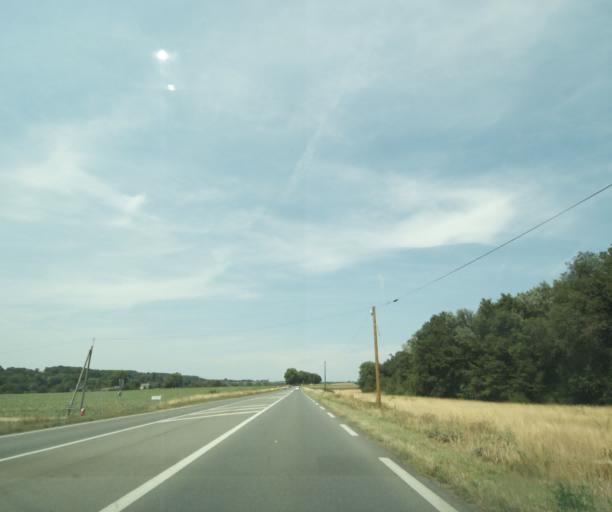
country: FR
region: Poitou-Charentes
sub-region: Departement de la Vienne
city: Antran
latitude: 46.8897
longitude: 0.5688
